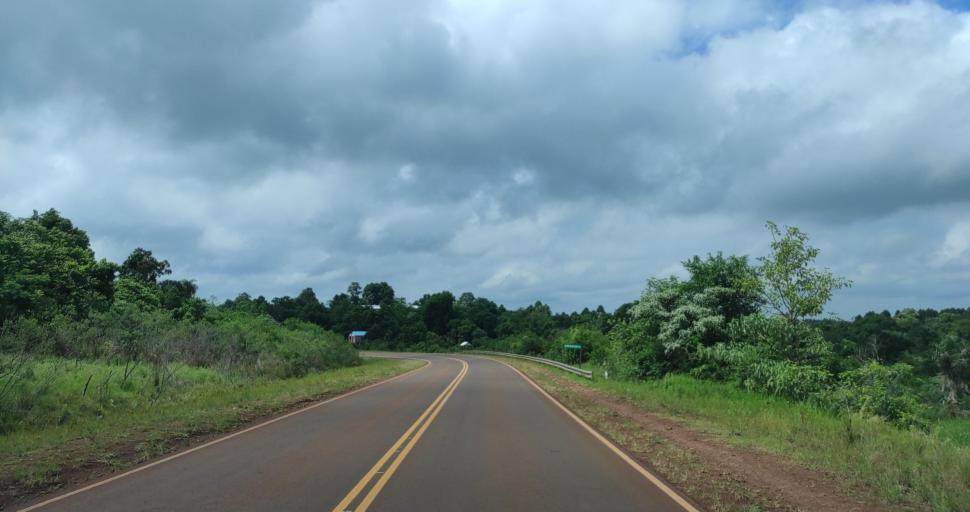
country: AR
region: Misiones
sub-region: Departamento de Veinticinco de Mayo
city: Veinticinco de Mayo
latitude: -27.3710
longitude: -54.8661
